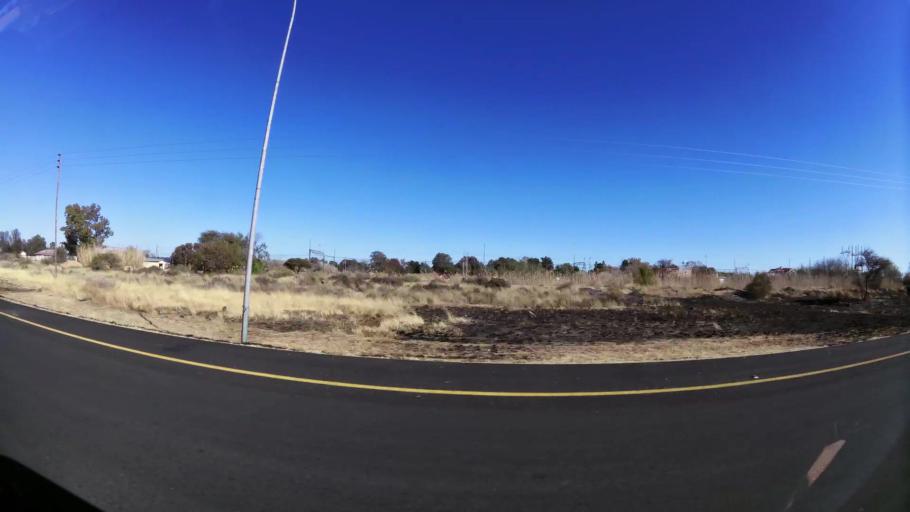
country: ZA
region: Northern Cape
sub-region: Frances Baard District Municipality
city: Kimberley
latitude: -28.6928
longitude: 24.7779
